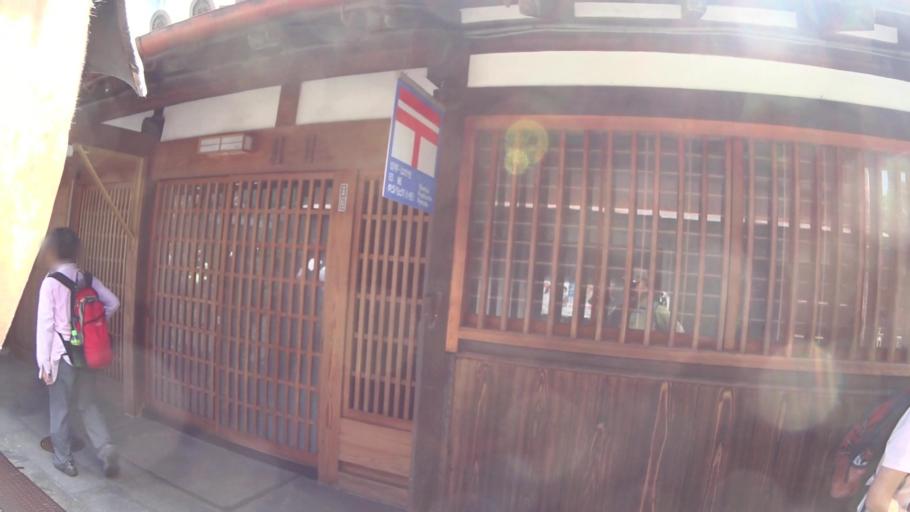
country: JP
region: Nara
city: Sakurai
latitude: 34.5127
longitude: 135.8524
